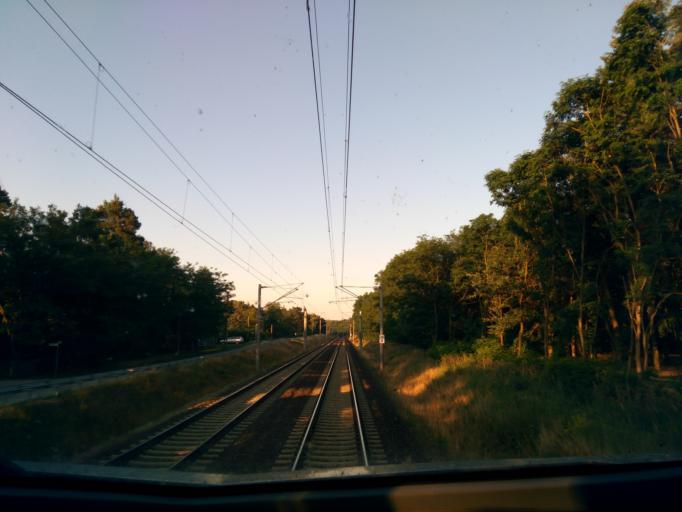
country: DE
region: Brandenburg
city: Bestensee
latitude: 52.2214
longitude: 13.6217
